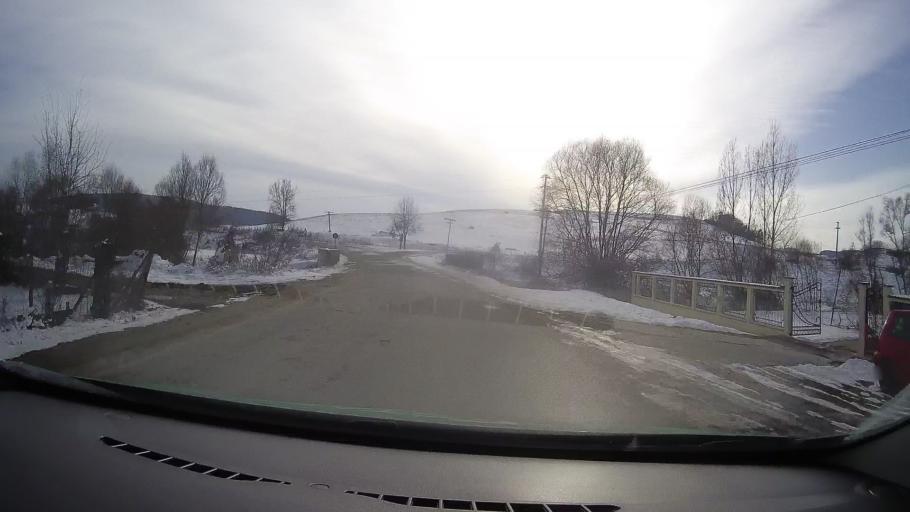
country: RO
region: Sibiu
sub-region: Oras Agnita
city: Ruja
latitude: 46.0021
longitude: 24.6729
